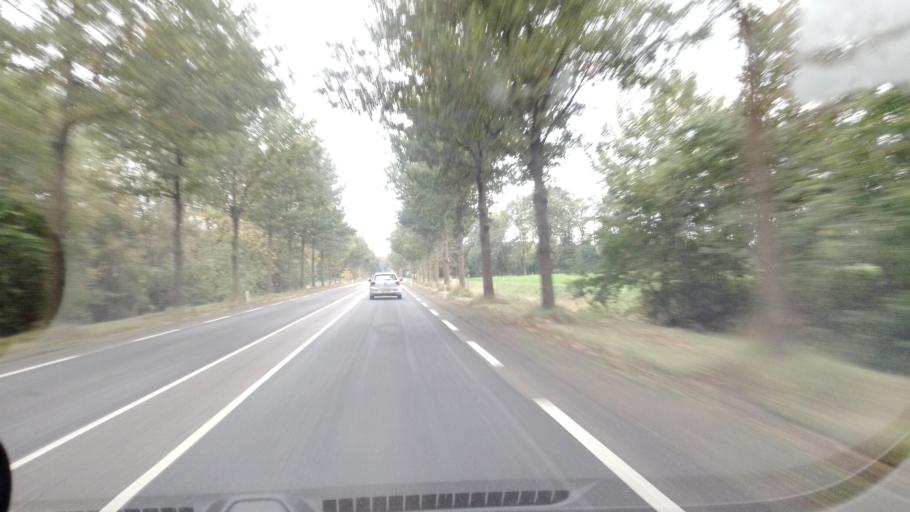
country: NL
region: Limburg
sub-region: Gemeente Venlo
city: Tegelen
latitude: 51.3551
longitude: 6.1174
